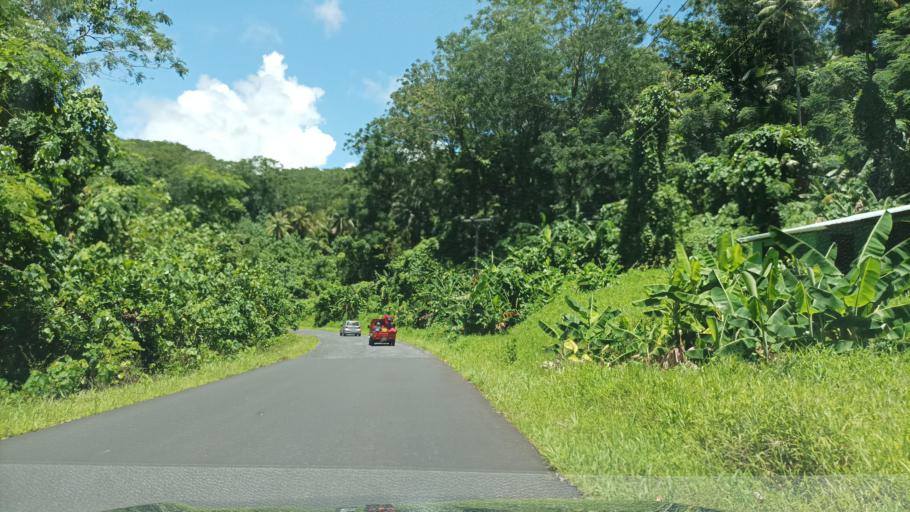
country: FM
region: Pohnpei
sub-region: Madolenihm Municipality
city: Madolenihm Municipality Government
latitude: 6.9175
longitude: 158.3217
